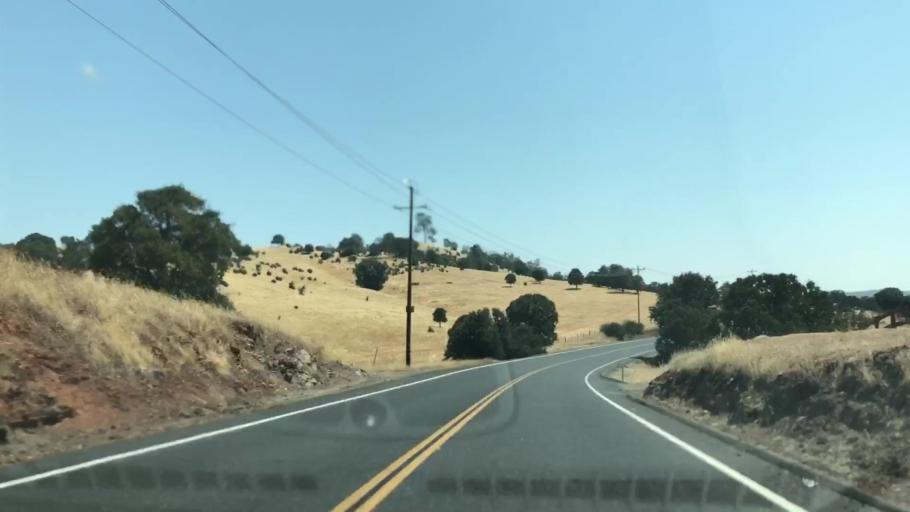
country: US
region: California
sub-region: Calaveras County
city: Copperopolis
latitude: 37.9279
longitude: -120.5976
